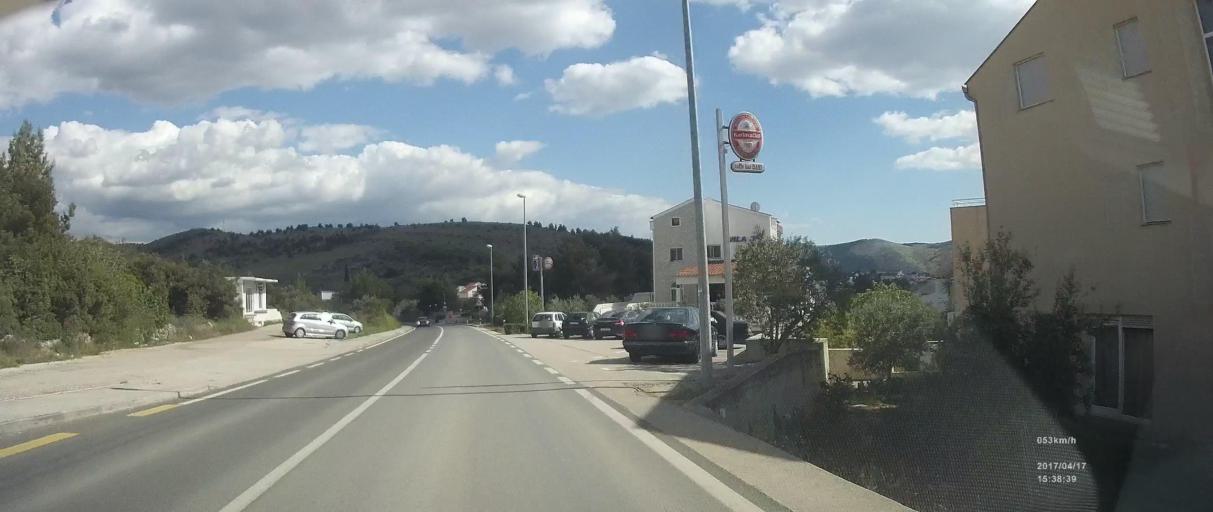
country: HR
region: Sibensko-Kniniska
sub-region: Grad Sibenik
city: Brodarica
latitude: 43.6627
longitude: 15.9451
